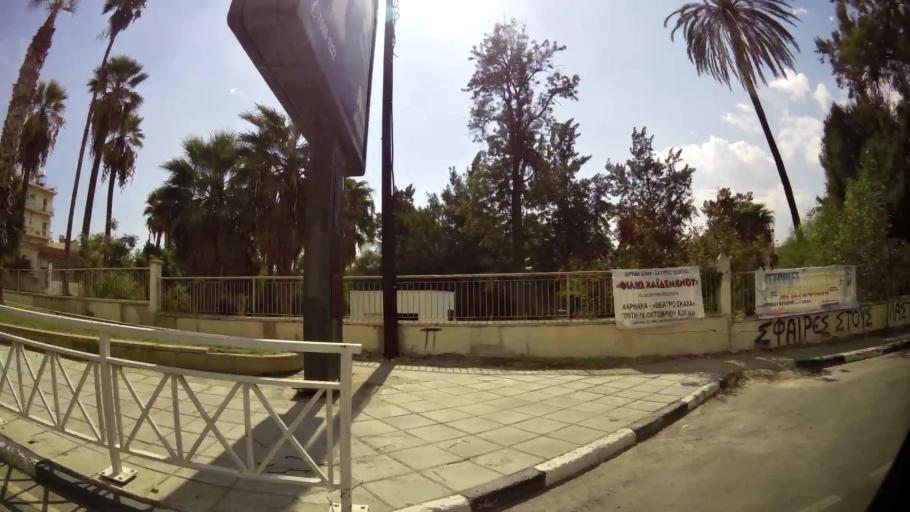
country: CY
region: Larnaka
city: Larnaca
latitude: 34.9163
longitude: 33.6250
